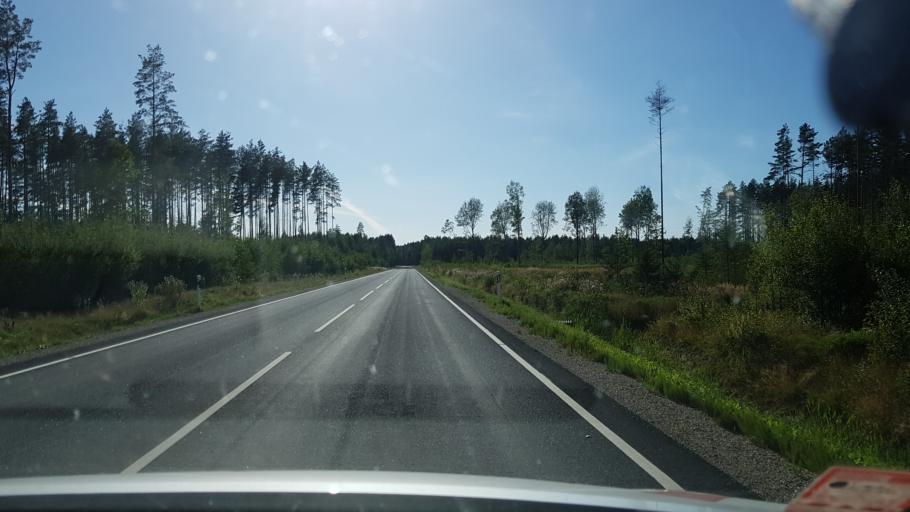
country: EE
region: Ida-Virumaa
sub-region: Kohtla-Nomme vald
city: Kohtla-Nomme
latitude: 59.0719
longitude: 27.1578
